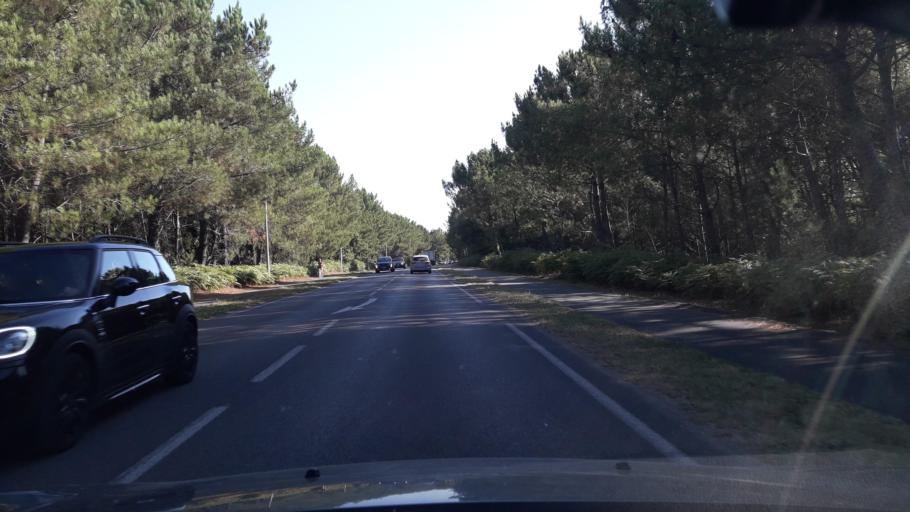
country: FR
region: Poitou-Charentes
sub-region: Departement de la Charente-Maritime
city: Les Mathes
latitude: 45.7056
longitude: -1.1646
